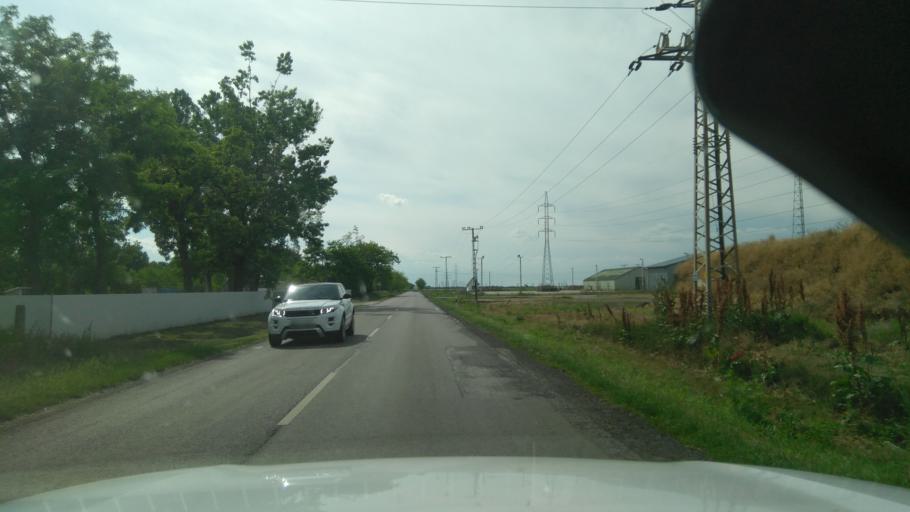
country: HU
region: Bekes
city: Medgyesegyhaza
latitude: 46.5055
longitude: 21.0107
